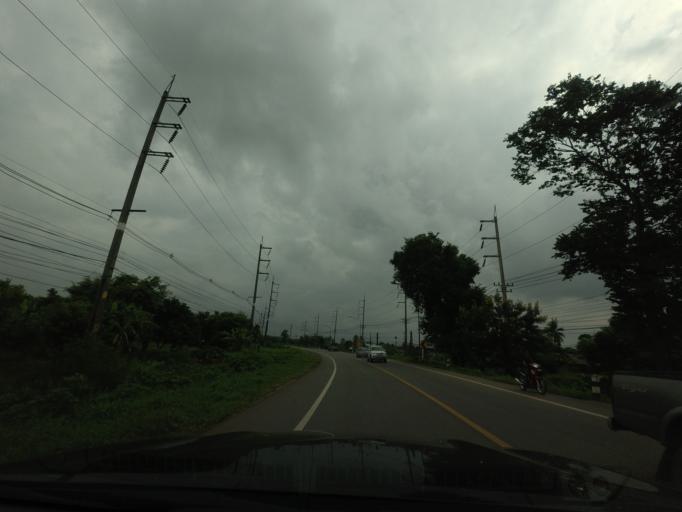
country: TH
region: Nong Khai
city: Tha Bo
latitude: 17.8938
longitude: 102.6001
